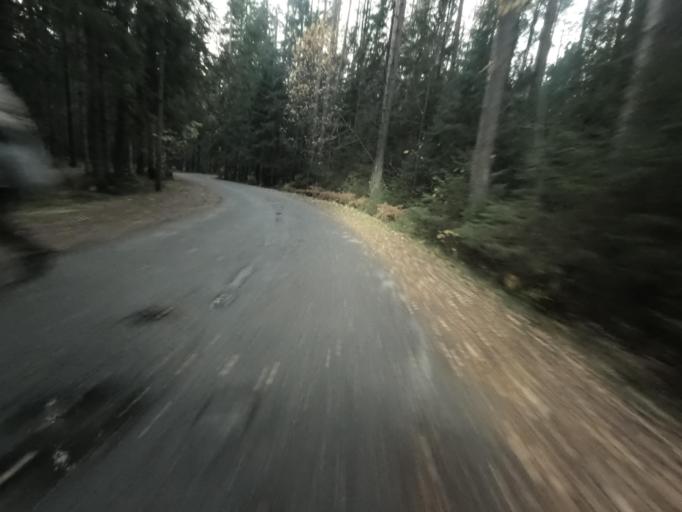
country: RU
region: St.-Petersburg
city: Komarovo
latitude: 60.2074
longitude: 29.7927
